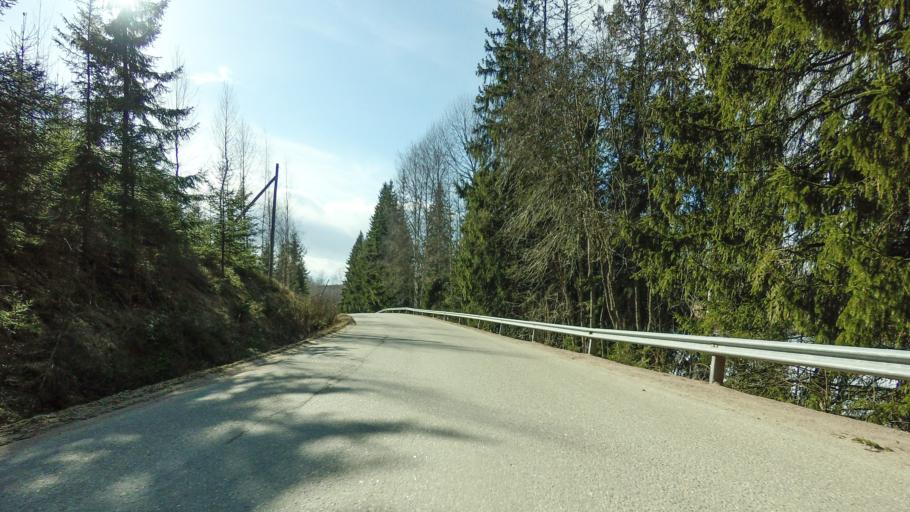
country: FI
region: Varsinais-Suomi
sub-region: Salo
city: Suomusjaervi
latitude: 60.3526
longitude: 23.6544
